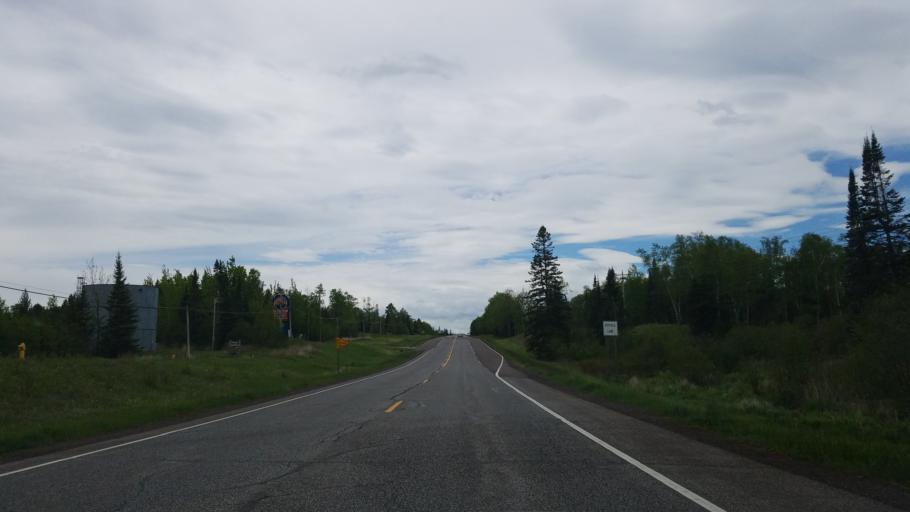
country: US
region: Minnesota
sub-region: Lake County
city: Two Harbors
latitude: 47.0365
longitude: -91.6463
